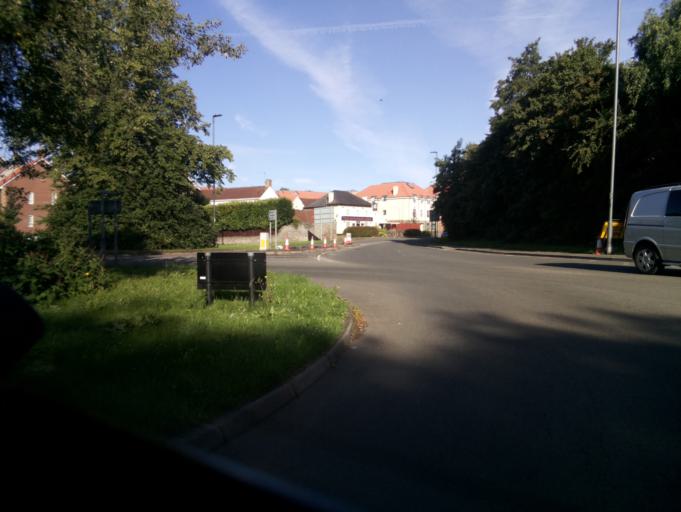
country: GB
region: England
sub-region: South Gloucestershire
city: Kingswood
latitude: 51.4413
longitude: -2.4974
